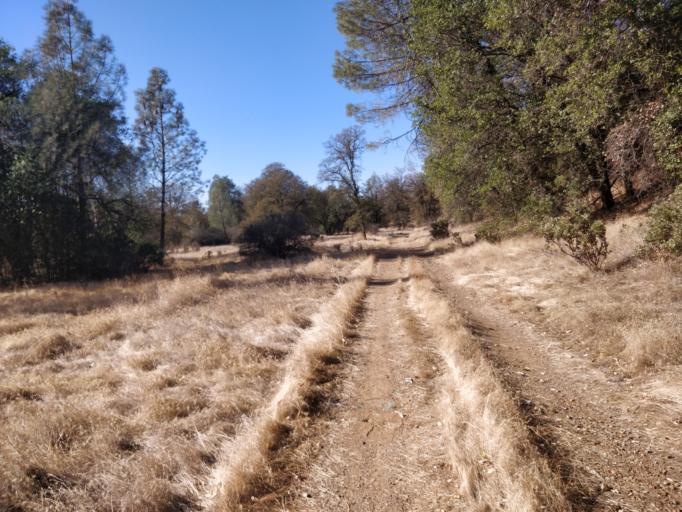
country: US
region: California
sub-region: Shasta County
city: Shasta Lake
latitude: 40.6240
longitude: -122.3222
